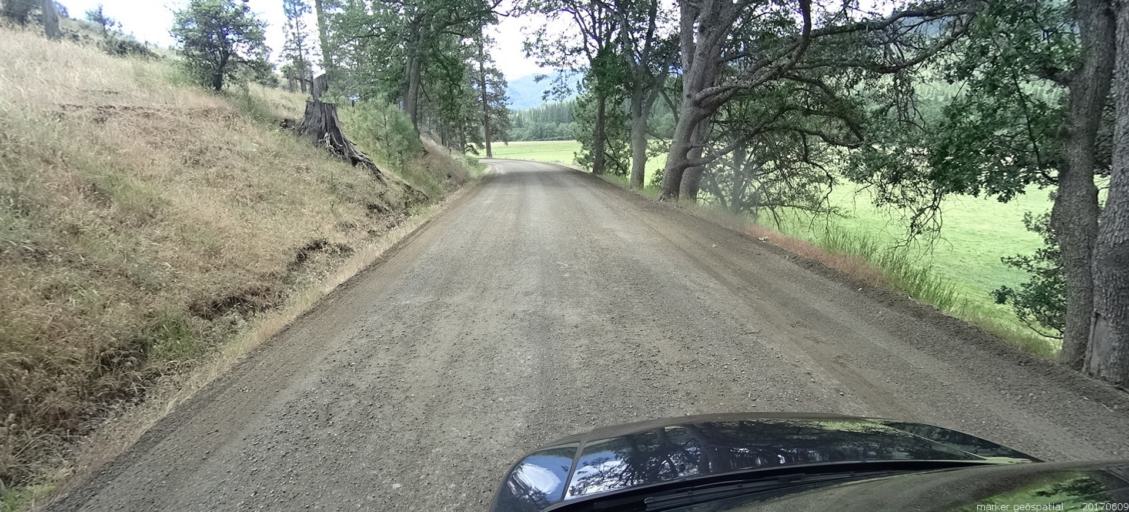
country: US
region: California
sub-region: Siskiyou County
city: Yreka
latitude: 41.3964
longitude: -122.8656
